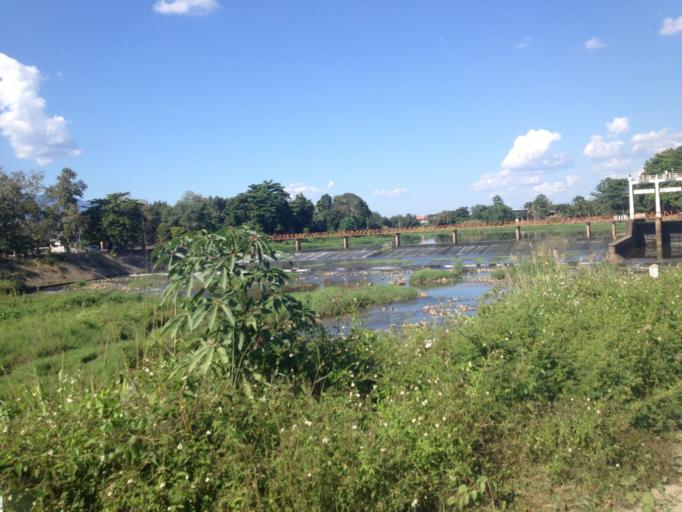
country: TH
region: Chiang Mai
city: Saraphi
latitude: 18.6892
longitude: 98.9872
